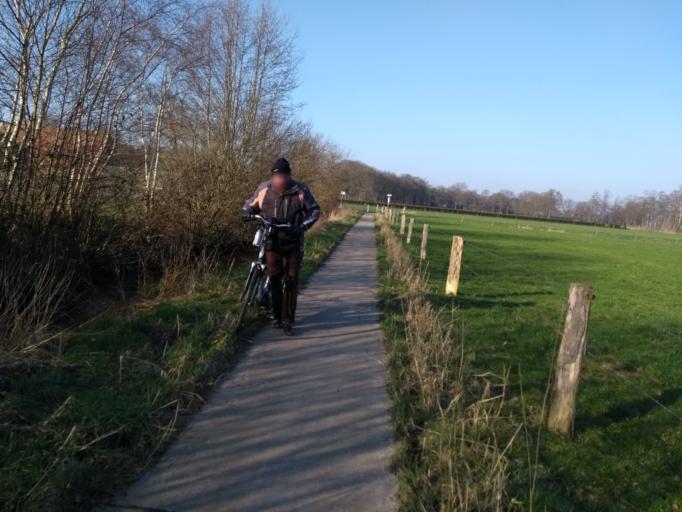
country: NL
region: Overijssel
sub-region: Gemeente Tubbergen
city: Tubbergen
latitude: 52.4015
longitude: 6.7357
